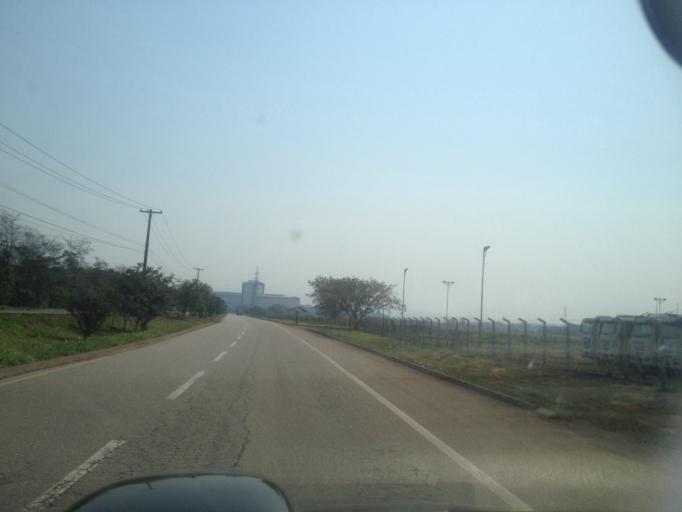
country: BR
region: Rio de Janeiro
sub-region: Porto Real
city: Porto Real
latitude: -22.4435
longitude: -44.3533
